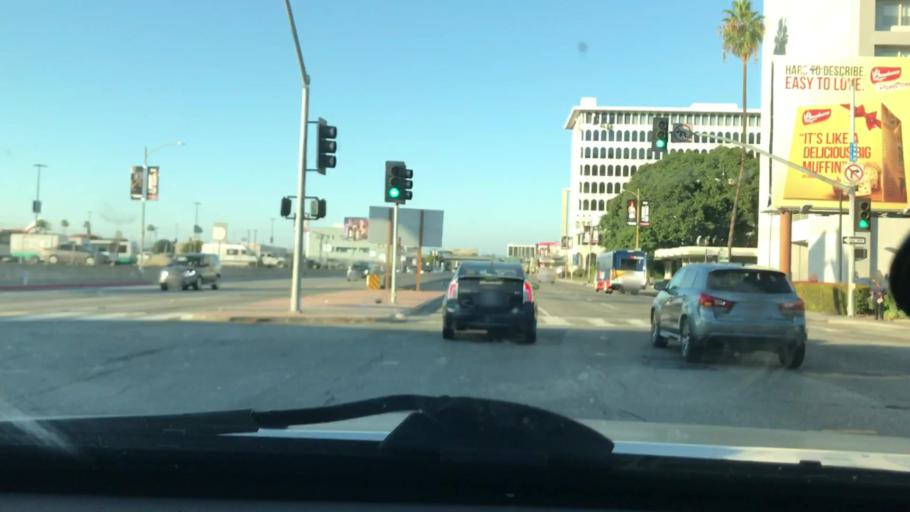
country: US
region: California
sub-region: Los Angeles County
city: El Segundo
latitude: 33.9454
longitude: -118.3962
